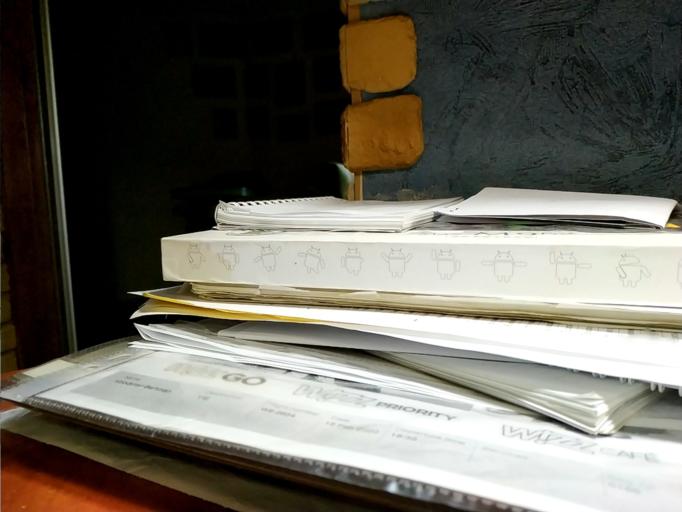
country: RU
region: Arkhangelskaya
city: Onega
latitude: 63.6042
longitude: 38.0843
